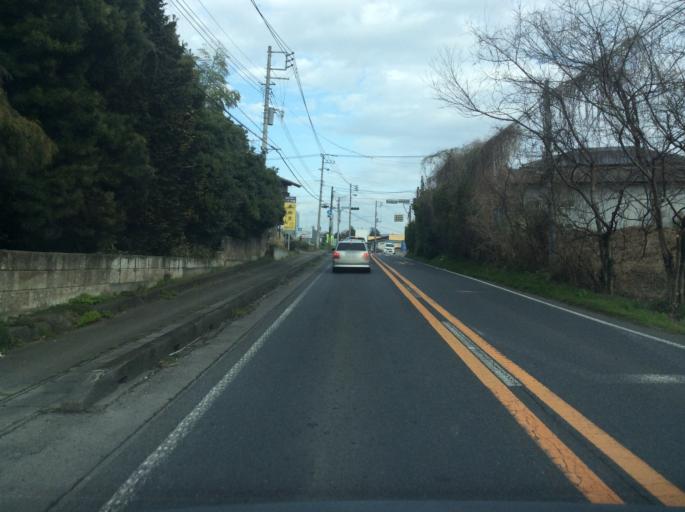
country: JP
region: Ibaraki
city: Tsukuba
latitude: 36.1819
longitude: 140.0391
